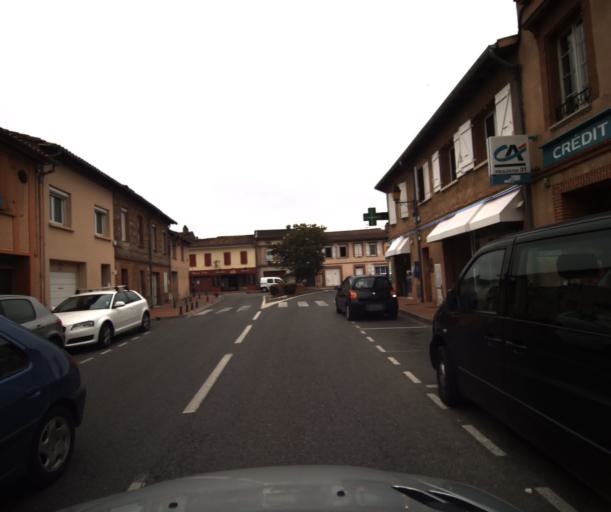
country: FR
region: Midi-Pyrenees
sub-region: Departement de la Haute-Garonne
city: Portet-sur-Garonne
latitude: 43.5241
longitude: 1.4073
